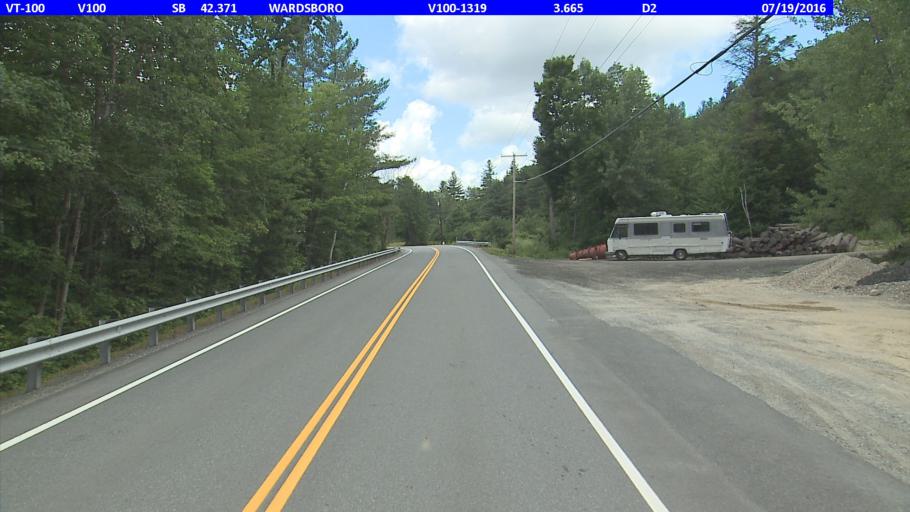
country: US
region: Vermont
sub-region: Windham County
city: Dover
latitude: 43.0507
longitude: -72.8584
